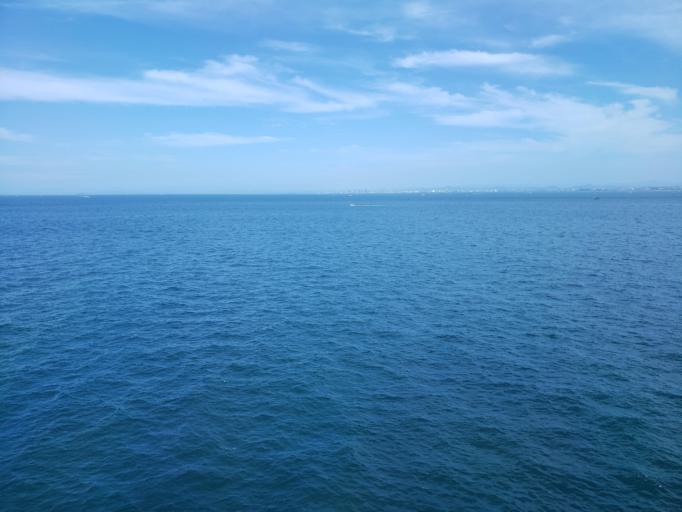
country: JP
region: Hyogo
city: Akashi
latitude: 34.6068
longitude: 134.9264
